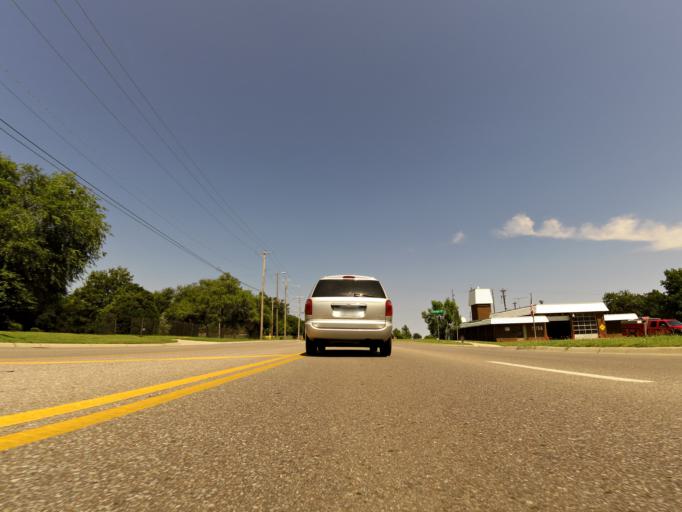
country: US
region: Kansas
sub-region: Sedgwick County
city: Bellaire
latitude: 37.7147
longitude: -97.2623
